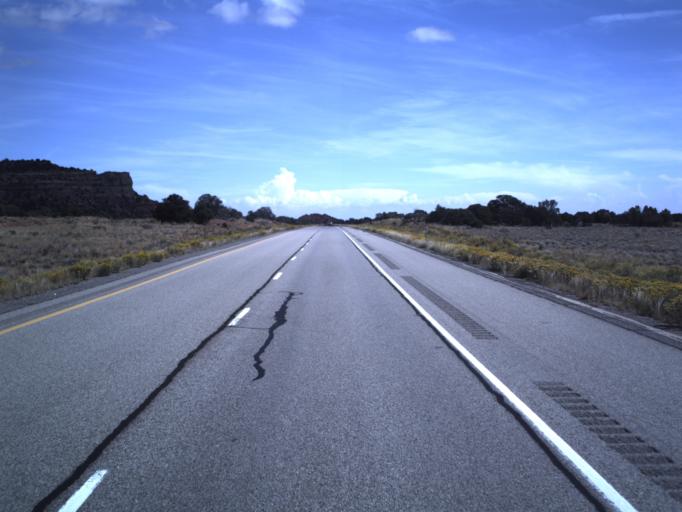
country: US
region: Utah
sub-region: Emery County
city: Castle Dale
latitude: 38.8710
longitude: -110.7286
